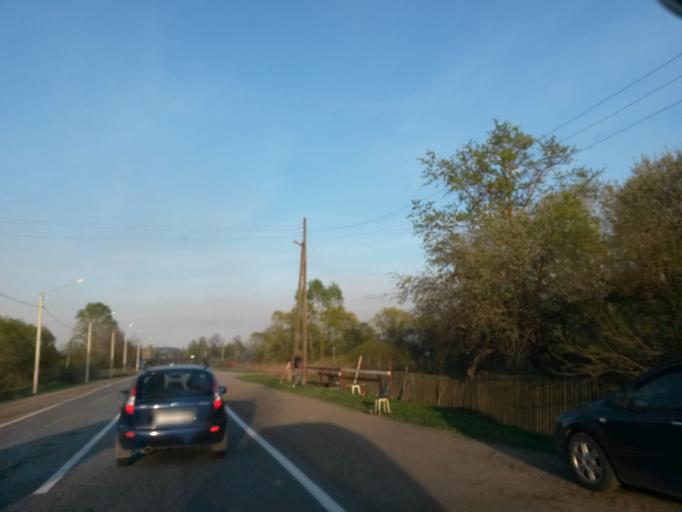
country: RU
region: Jaroslavl
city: Kurba
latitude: 57.6787
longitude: 39.5739
